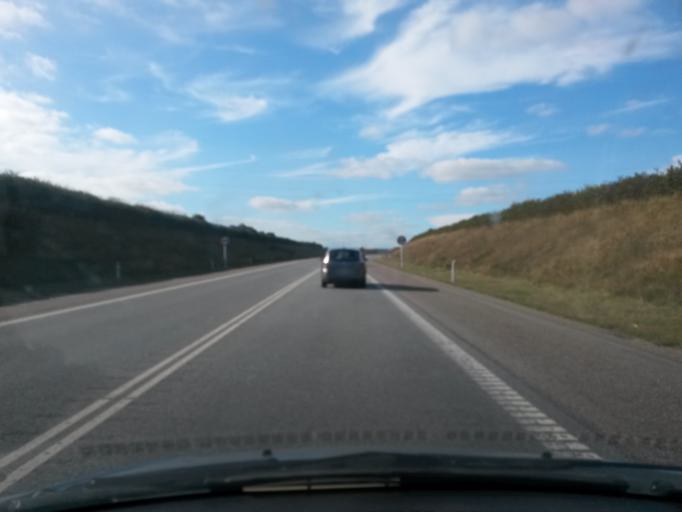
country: DK
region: Central Jutland
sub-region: Herning Kommune
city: Snejbjerg
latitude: 56.1885
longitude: 8.9114
